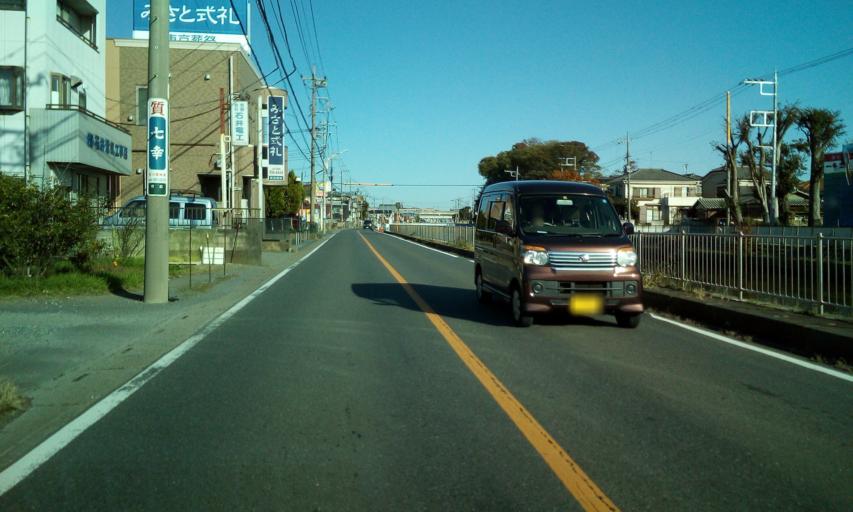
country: JP
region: Chiba
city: Nagareyama
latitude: 35.8246
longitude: 139.8830
